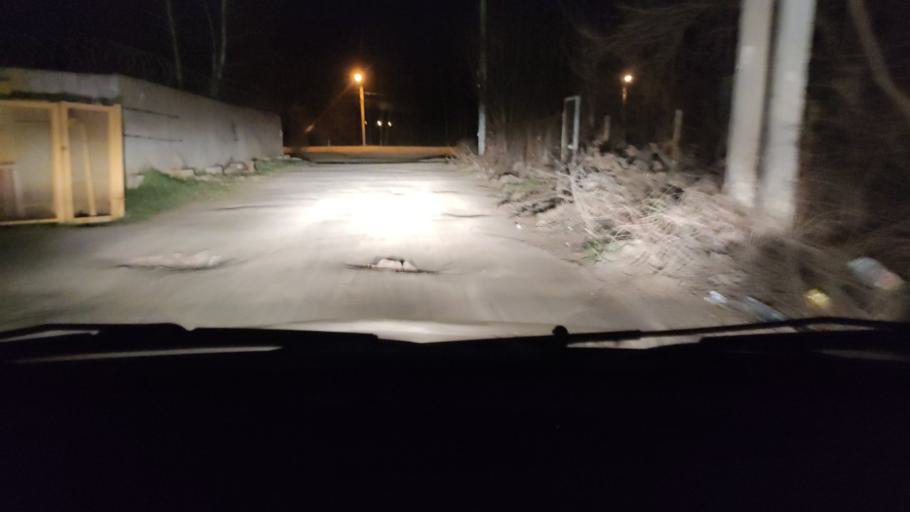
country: RU
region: Voronezj
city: Pridonskoy
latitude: 51.6381
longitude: 39.0866
